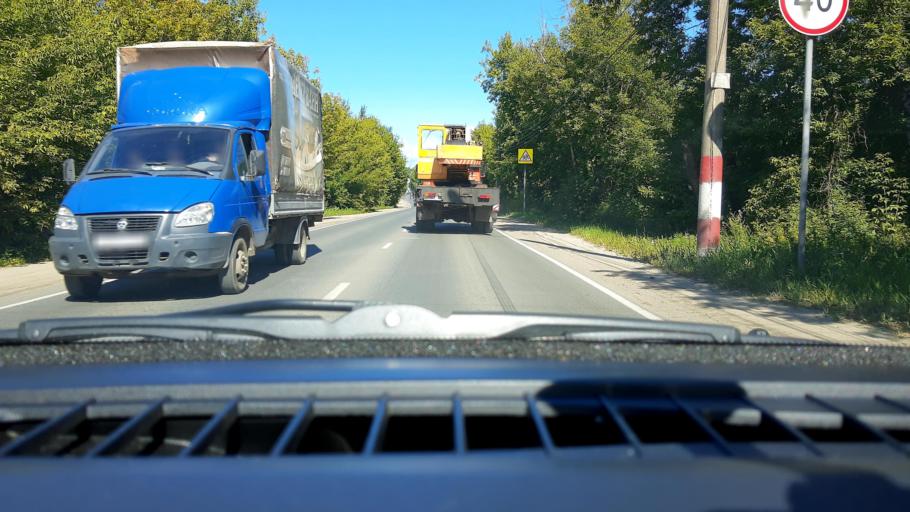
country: RU
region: Nizjnij Novgorod
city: Bor
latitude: 56.3589
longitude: 44.0894
